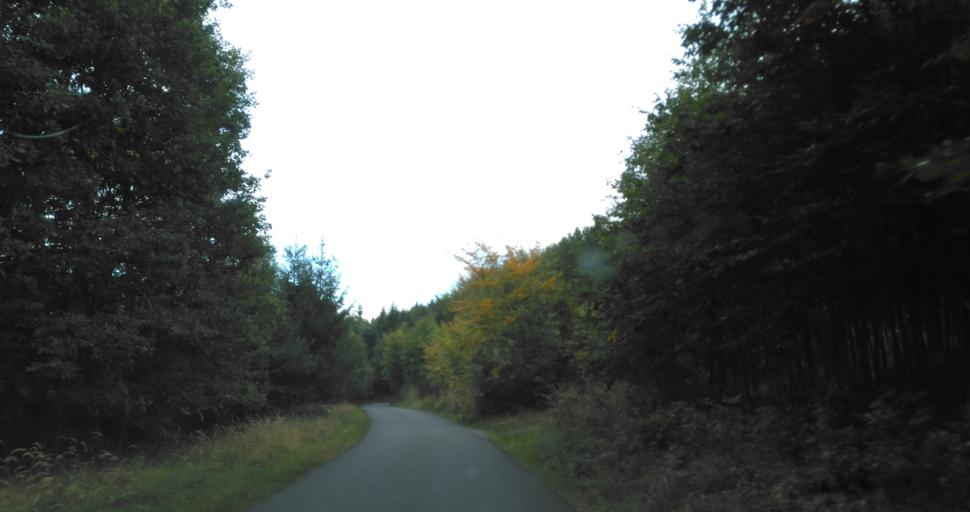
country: CZ
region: Plzensky
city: Zbiroh
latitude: 49.9368
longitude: 13.7803
